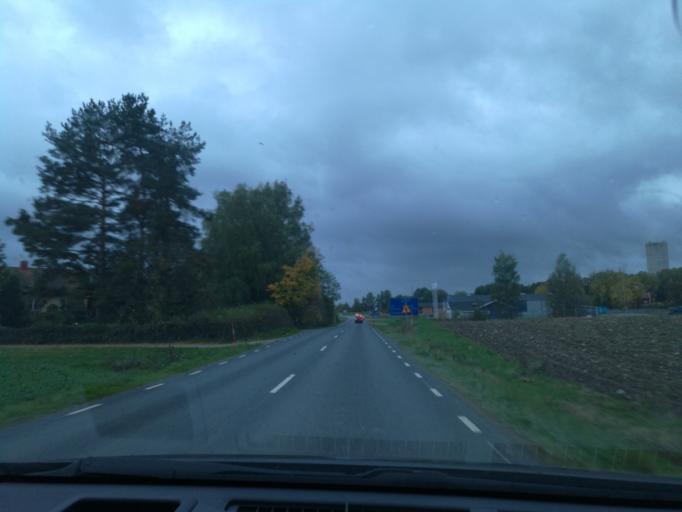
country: SE
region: Soedermanland
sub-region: Vingakers Kommun
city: Vingaker
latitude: 59.0629
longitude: 15.8835
